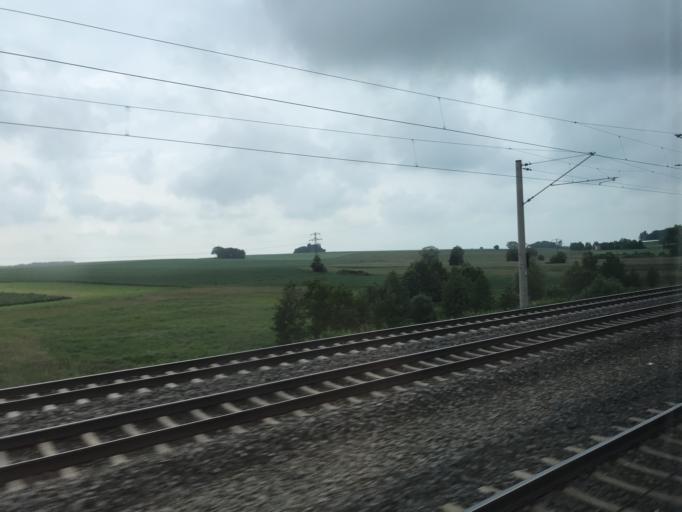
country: DE
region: Bavaria
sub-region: Upper Bavaria
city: Althegnenberg
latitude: 48.2406
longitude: 11.0519
